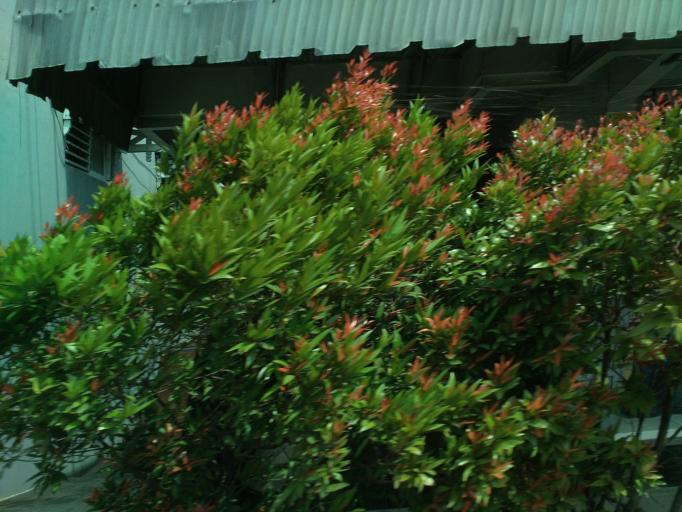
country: ID
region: Central Java
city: Wedi
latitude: -7.7176
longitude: 110.5830
